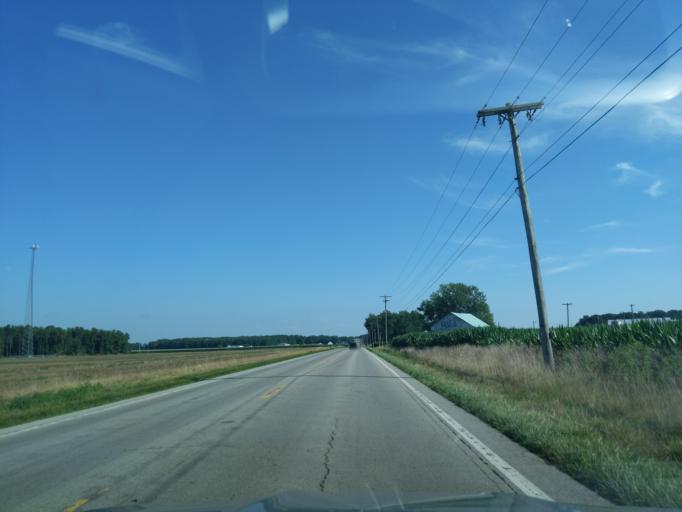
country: US
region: Indiana
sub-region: Ripley County
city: Osgood
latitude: 39.1653
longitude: -85.3095
